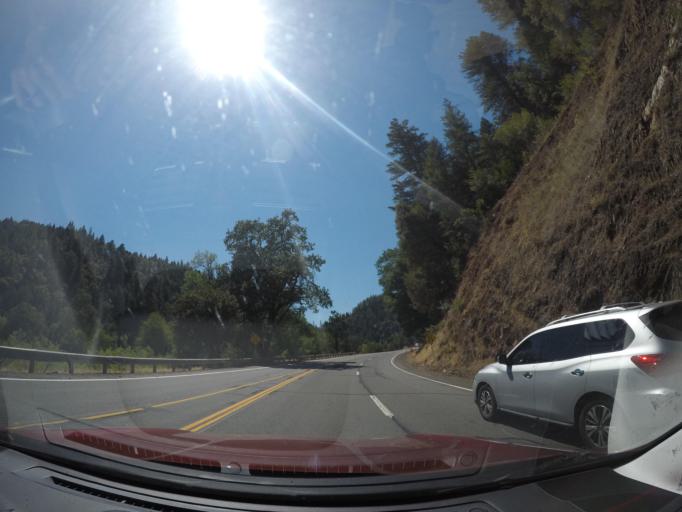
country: US
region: California
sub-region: Shasta County
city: Bella Vista
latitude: 40.7508
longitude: -122.0395
